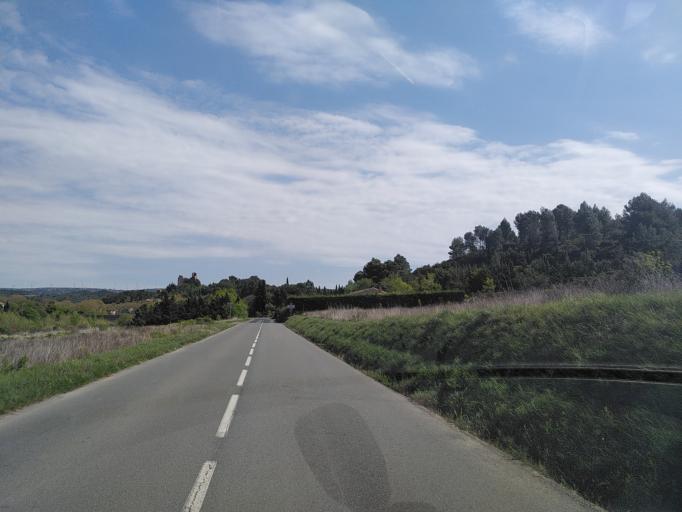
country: FR
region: Languedoc-Roussillon
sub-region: Departement de l'Aude
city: Portel-des-Corbieres
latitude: 42.9922
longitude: 2.8074
